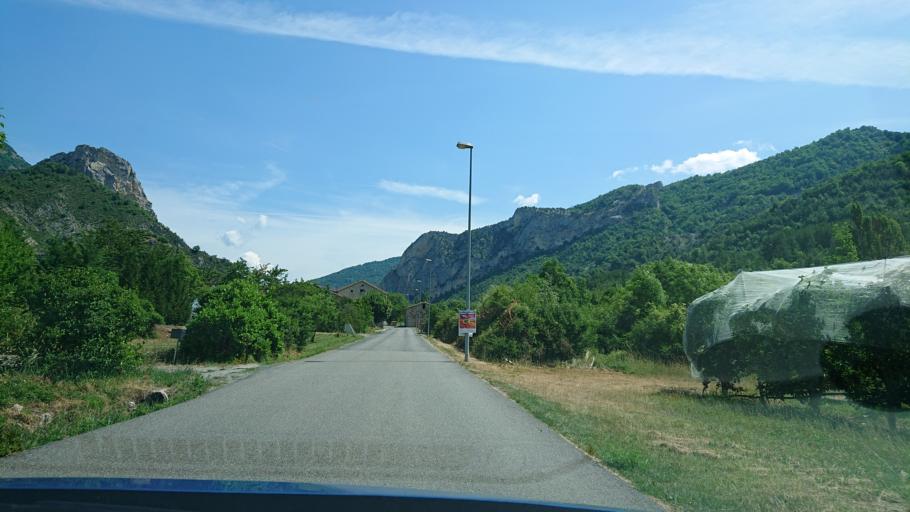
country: FR
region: Provence-Alpes-Cote d'Azur
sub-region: Departement des Hautes-Alpes
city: Tallard
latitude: 44.3673
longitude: 6.0574
